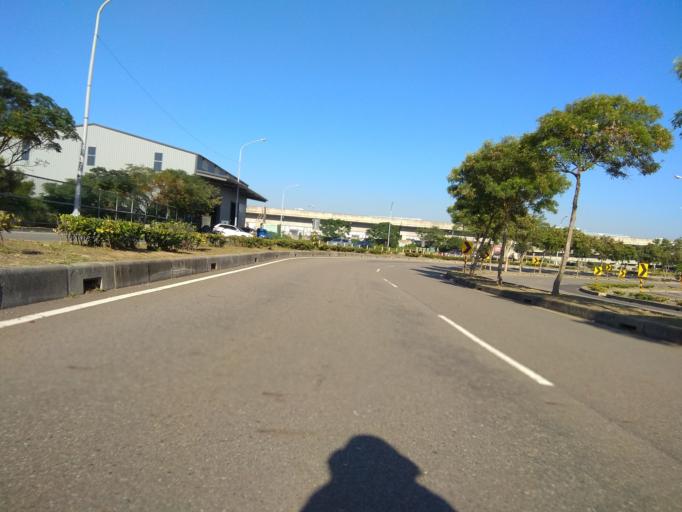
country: TW
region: Taiwan
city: Taoyuan City
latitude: 25.0251
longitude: 121.2179
